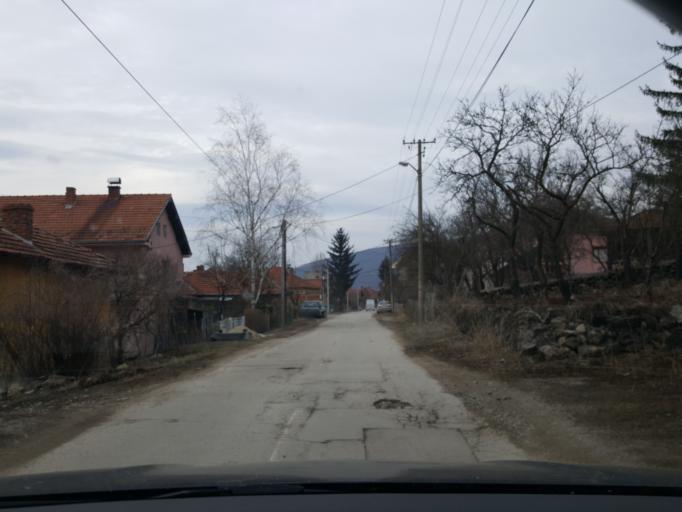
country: RS
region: Central Serbia
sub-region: Pirotski Okrug
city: Dimitrovgrad
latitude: 43.0040
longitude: 22.7617
